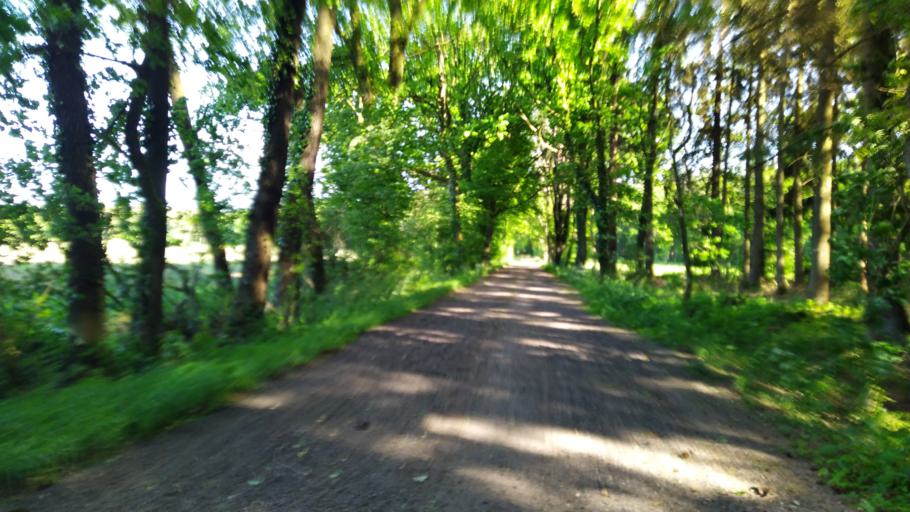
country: DE
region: Lower Saxony
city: Ahlerstedt
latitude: 53.4224
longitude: 9.4795
